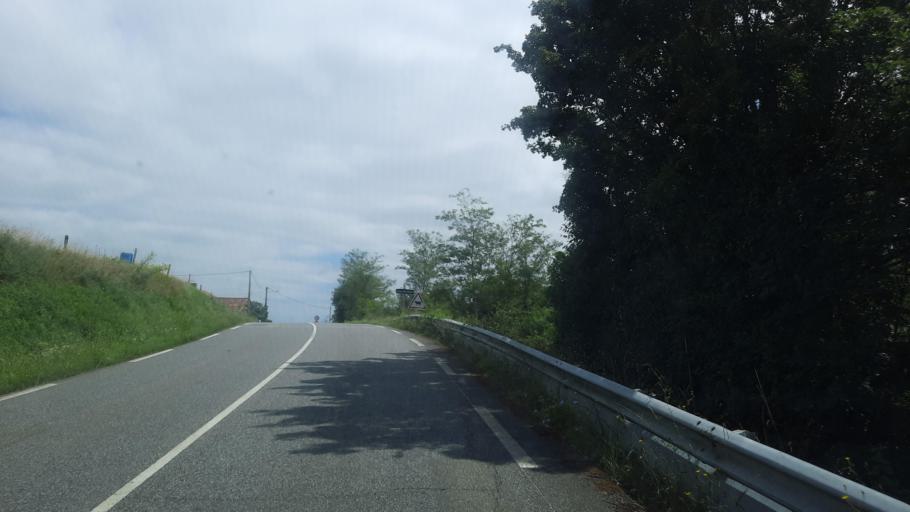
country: FR
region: Midi-Pyrenees
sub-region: Departement des Hautes-Pyrenees
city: Trie-sur-Baise
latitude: 43.3000
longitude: 0.2877
